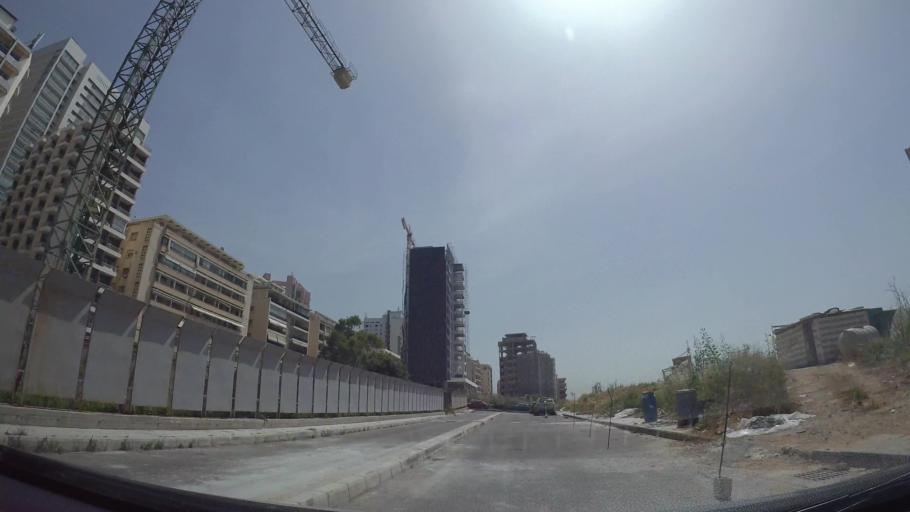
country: LB
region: Beyrouth
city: Ra's Bayrut
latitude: 33.8944
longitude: 35.4727
